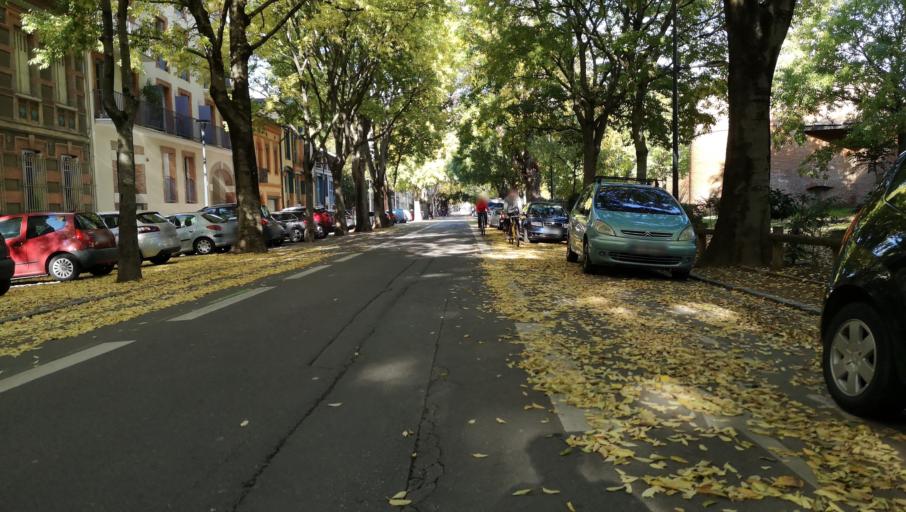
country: FR
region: Midi-Pyrenees
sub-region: Departement de la Haute-Garonne
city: Toulouse
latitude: 43.6073
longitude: 1.4348
